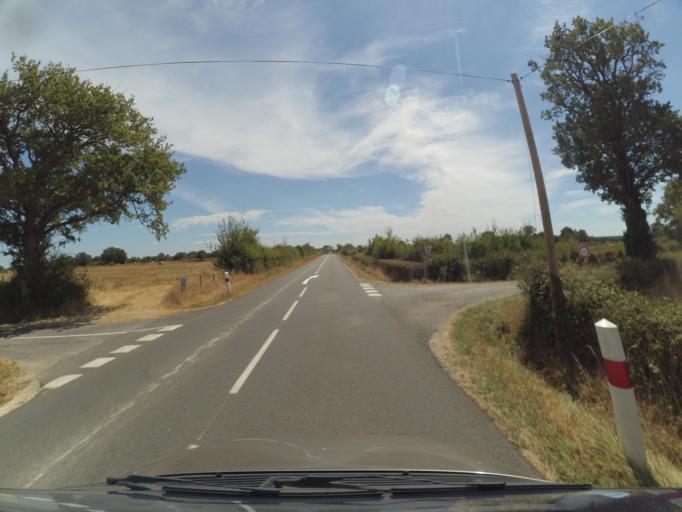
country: FR
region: Poitou-Charentes
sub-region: Departement de la Vienne
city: Availles-Limouzine
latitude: 46.1468
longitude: 0.5551
